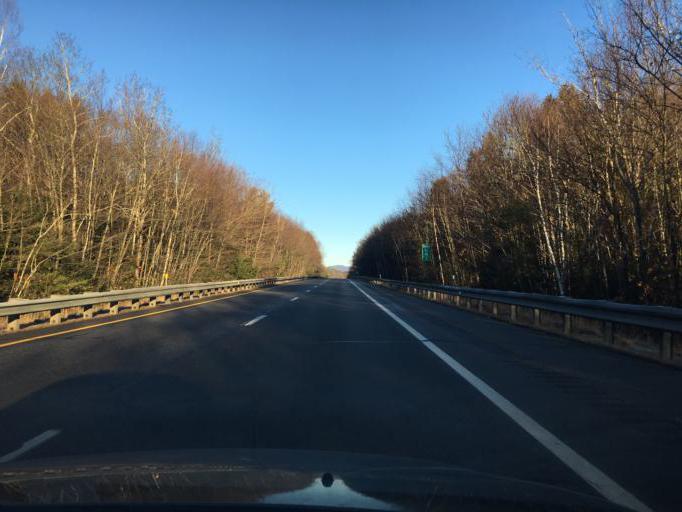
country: US
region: New Hampshire
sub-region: Belknap County
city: Sanbornton
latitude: 43.4779
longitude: -71.5869
